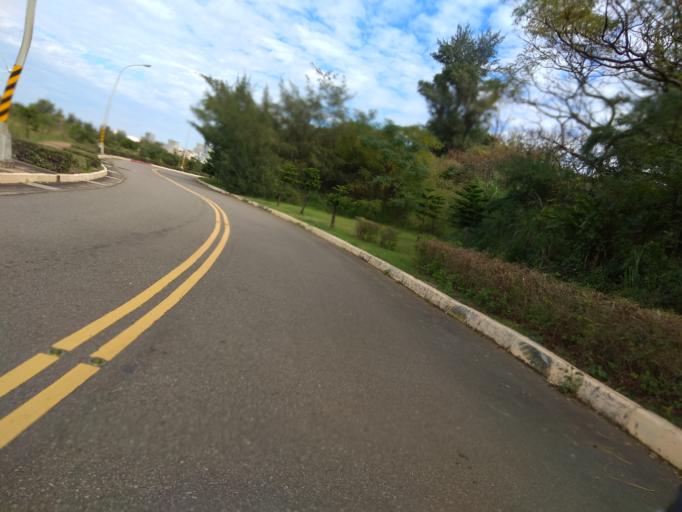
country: TW
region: Taiwan
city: Taoyuan City
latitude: 25.0449
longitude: 121.0867
